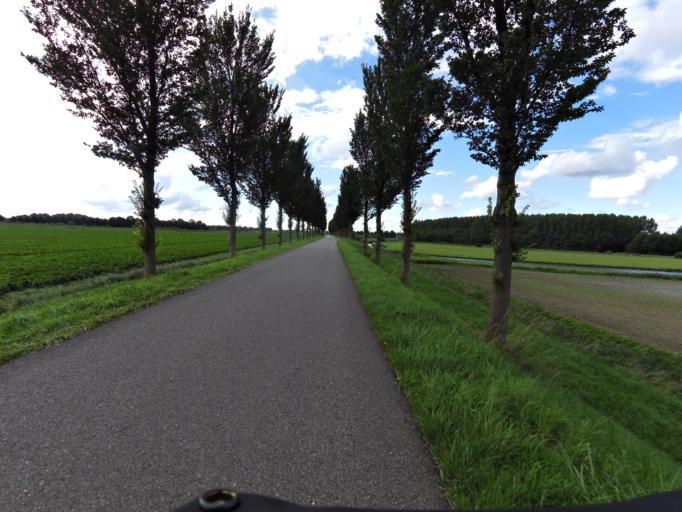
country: NL
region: North Brabant
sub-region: Gemeente Steenbergen
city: Nieuw-Vossemeer
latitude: 51.6795
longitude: 4.2196
